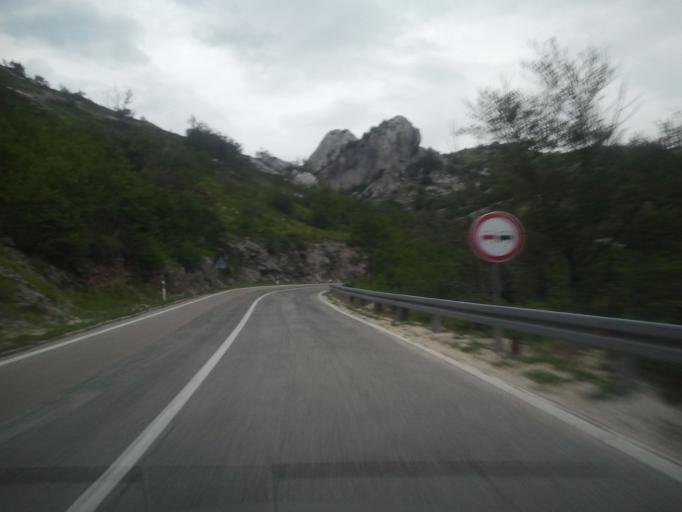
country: HR
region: Zadarska
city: Gracac
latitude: 44.2434
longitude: 15.8113
